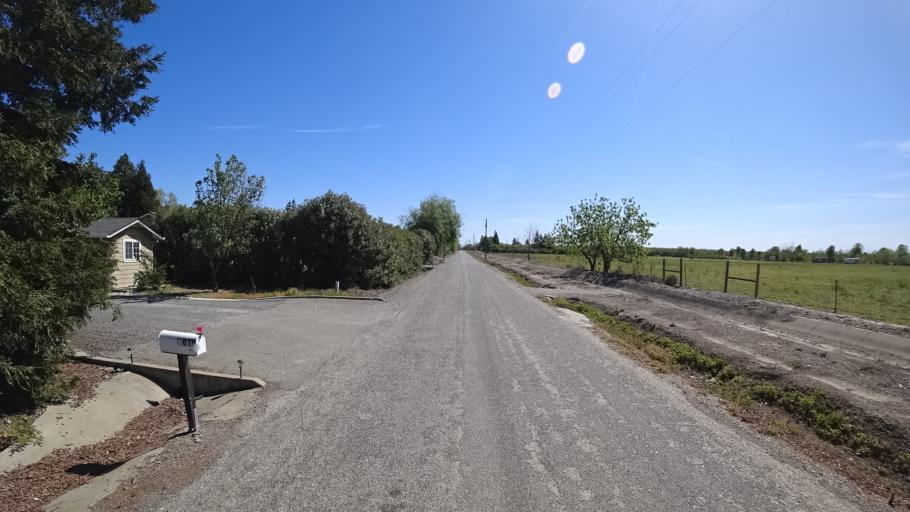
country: US
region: California
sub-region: Glenn County
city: Orland
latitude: 39.7432
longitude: -122.1398
